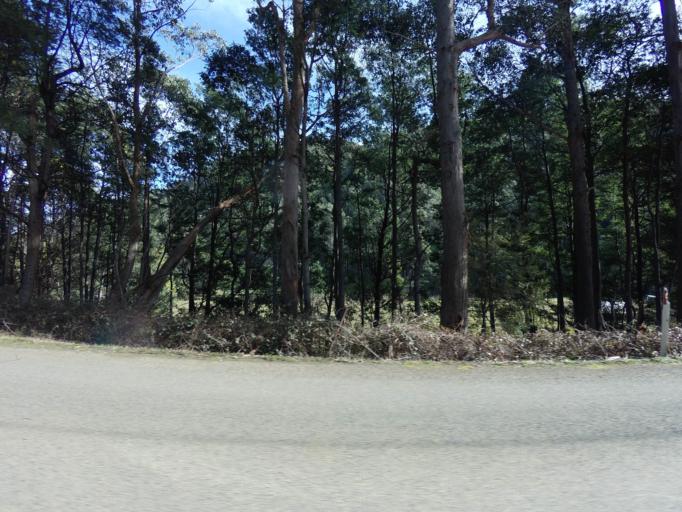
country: AU
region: Tasmania
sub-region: Huon Valley
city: Huonville
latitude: -43.0371
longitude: 147.1394
